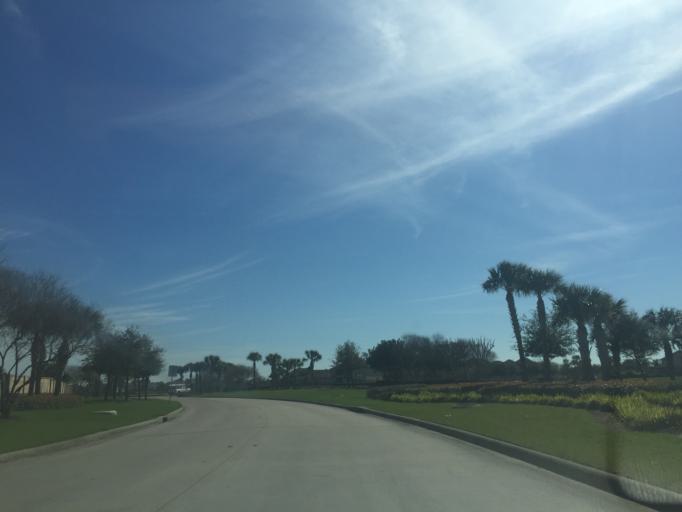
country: US
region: Texas
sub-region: Galveston County
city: Kemah
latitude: 29.5146
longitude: -95.0218
